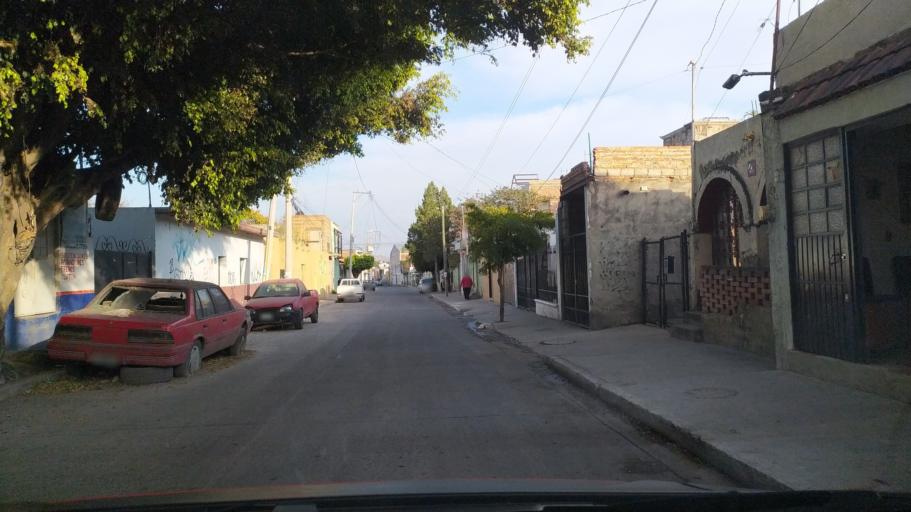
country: MX
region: Jalisco
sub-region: Tlajomulco de Zuniga
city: Palomar
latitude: 20.6214
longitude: -103.4555
